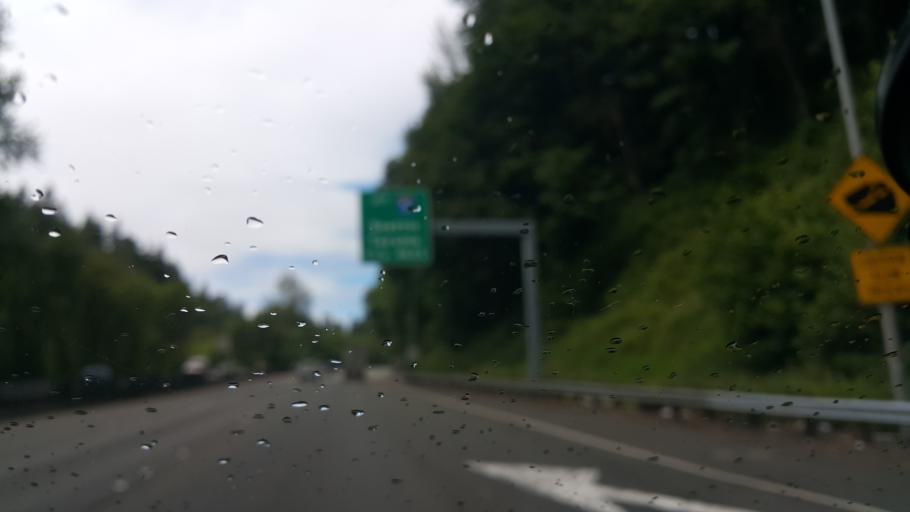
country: US
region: Washington
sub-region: King County
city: Algona
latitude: 47.3040
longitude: -122.2639
